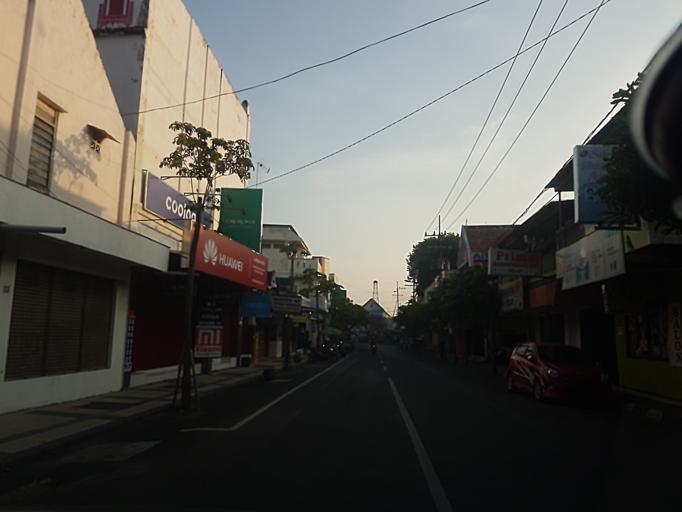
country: ID
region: East Java
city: Gresik
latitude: -7.1555
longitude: 112.6561
